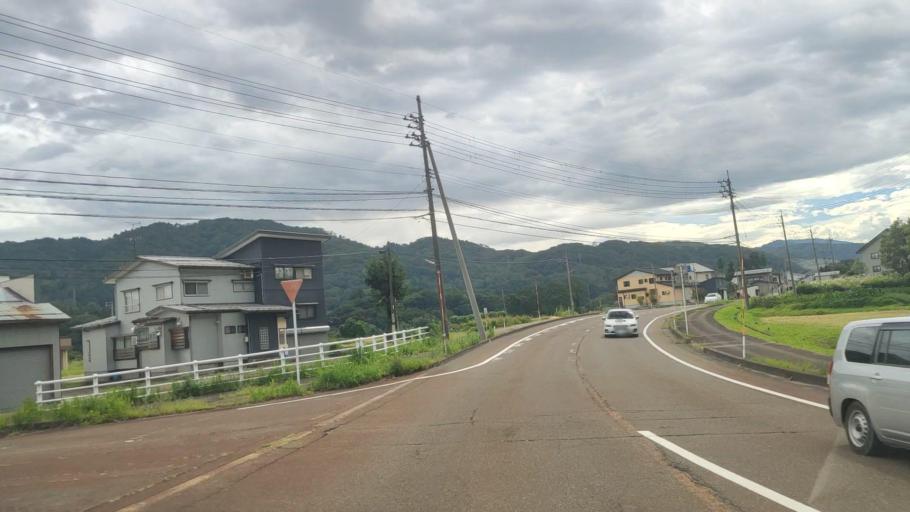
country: JP
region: Niigata
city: Arai
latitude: 37.0050
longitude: 138.2619
